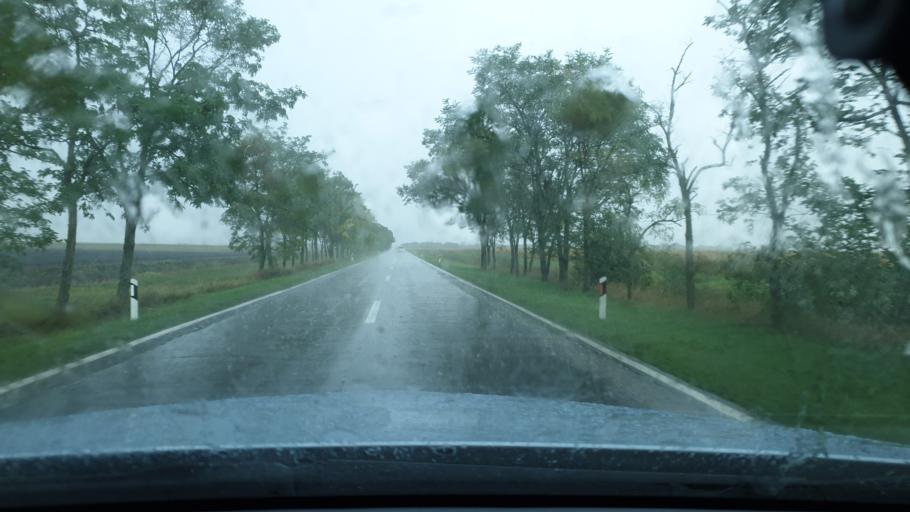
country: RS
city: Lazarevo
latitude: 45.3909
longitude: 20.5615
